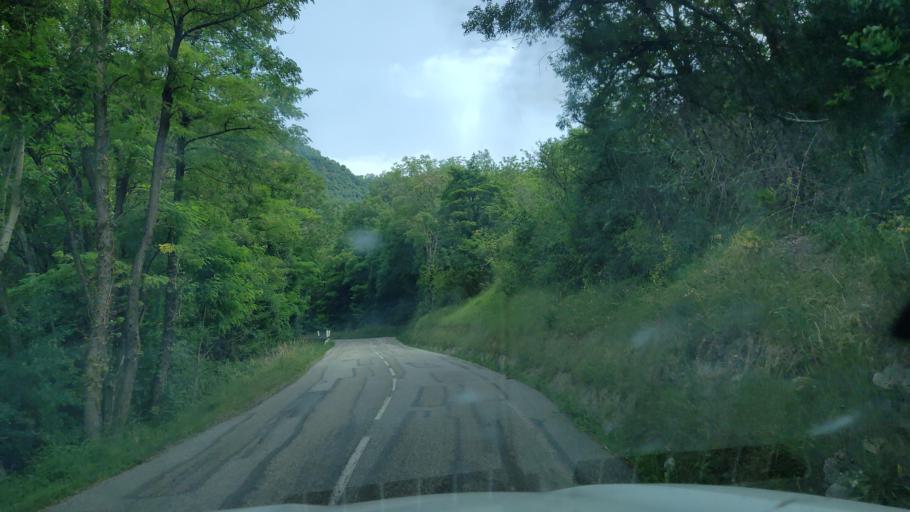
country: FR
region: Rhone-Alpes
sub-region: Departement de la Savoie
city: Challes-les-Eaux
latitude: 45.5435
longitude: 6.0068
